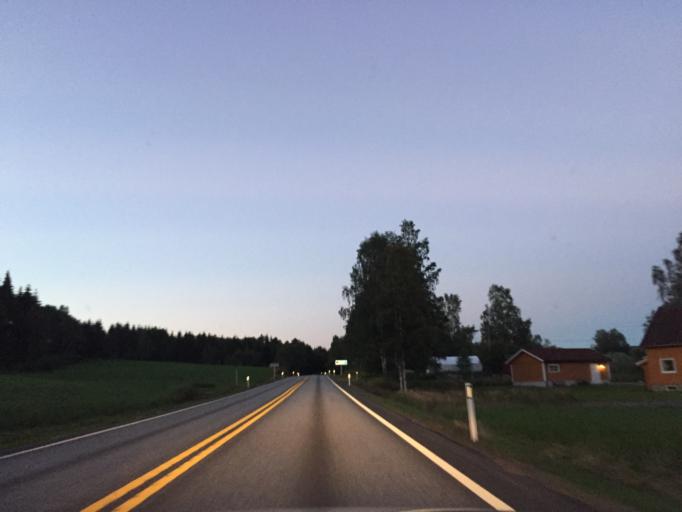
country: NO
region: Hedmark
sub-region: Kongsvinger
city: Spetalen
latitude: 60.2112
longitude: 11.9107
